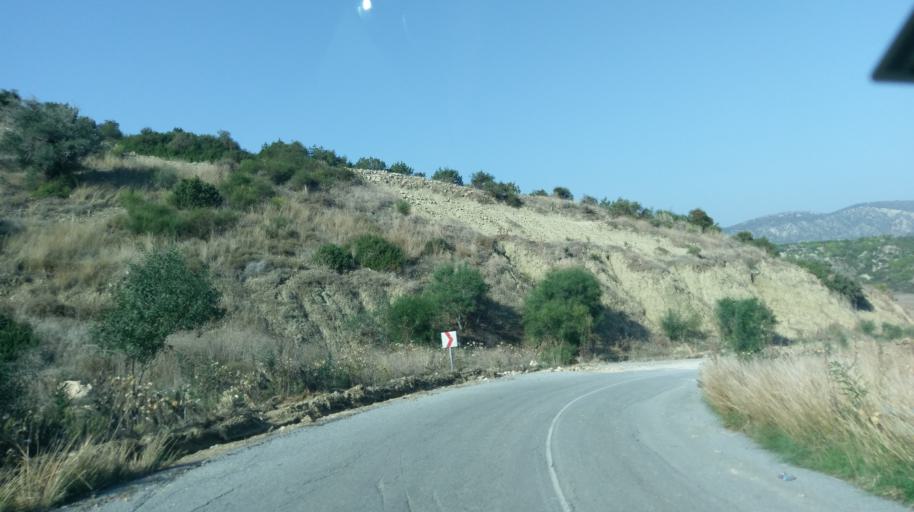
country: CY
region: Ammochostos
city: Leonarisso
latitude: 35.4962
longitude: 34.2252
